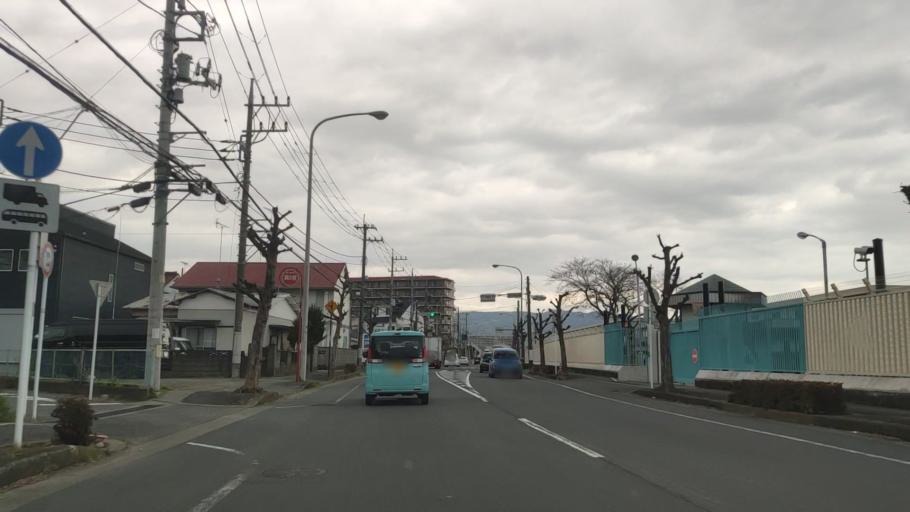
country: JP
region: Kanagawa
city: Odawara
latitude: 35.2736
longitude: 139.1890
